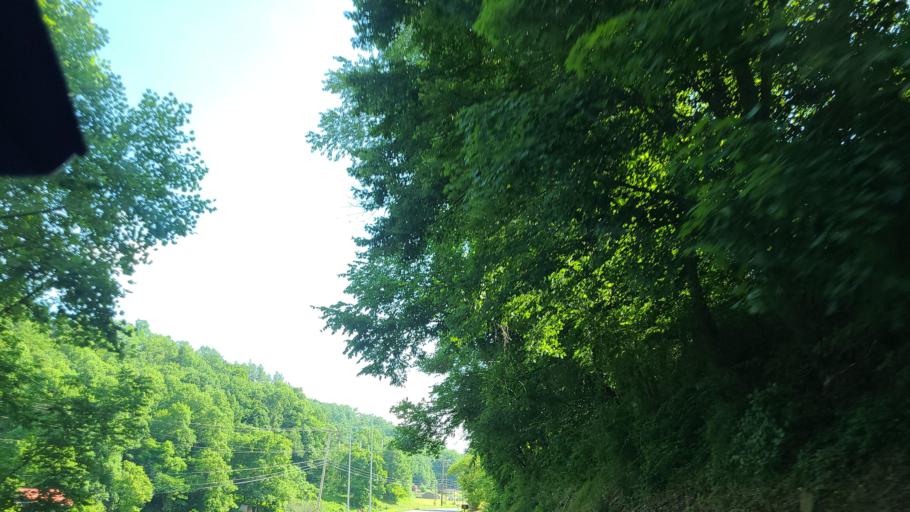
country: US
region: Kentucky
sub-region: Bell County
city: Pineville
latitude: 36.7624
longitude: -83.7795
